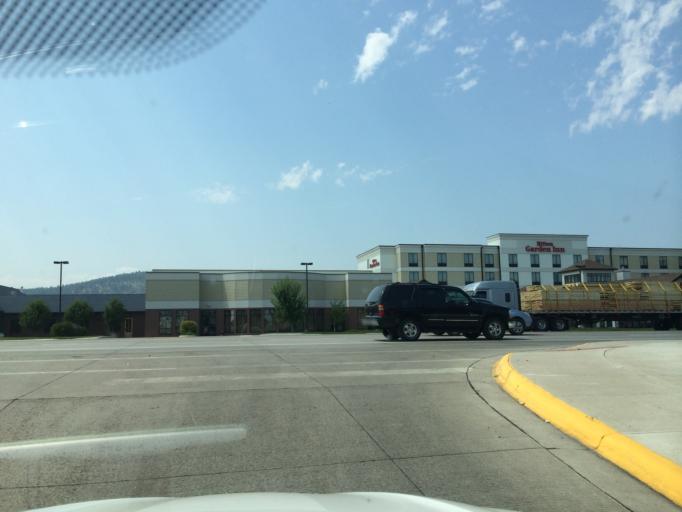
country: US
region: Montana
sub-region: Flathead County
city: Kalispell
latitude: 48.1808
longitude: -114.3032
